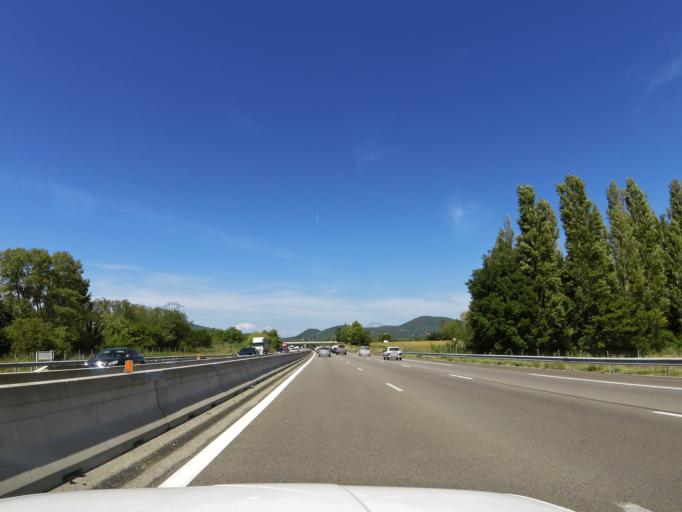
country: FR
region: Rhone-Alpes
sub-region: Departement de la Drome
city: Montboucher-sur-Jabron
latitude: 44.5671
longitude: 4.8102
